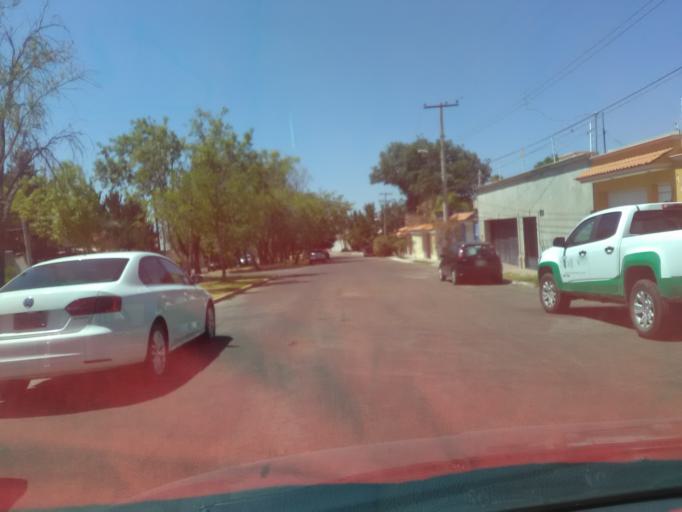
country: MX
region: Durango
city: Victoria de Durango
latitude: 24.0157
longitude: -104.6806
